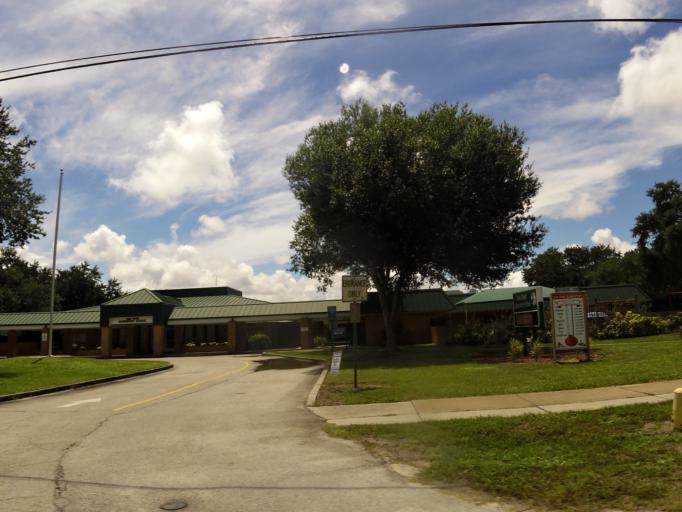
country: US
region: Florida
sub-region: Brevard County
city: Mims
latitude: 28.6372
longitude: -80.8518
